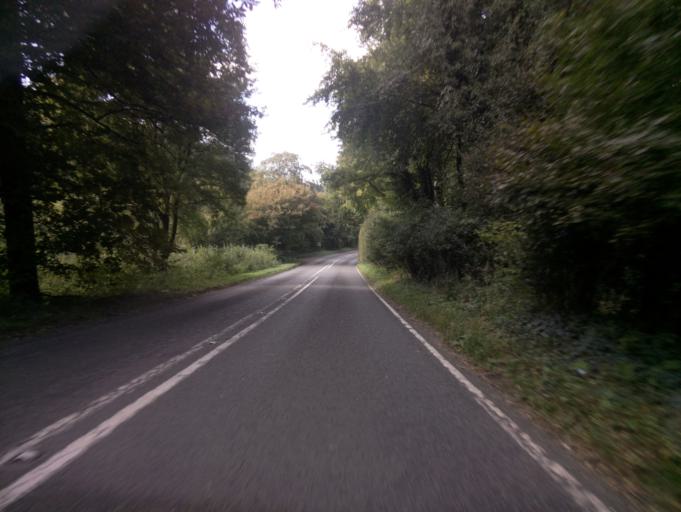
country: GB
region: England
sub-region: Hampshire
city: Basingstoke
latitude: 51.2225
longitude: -1.0635
